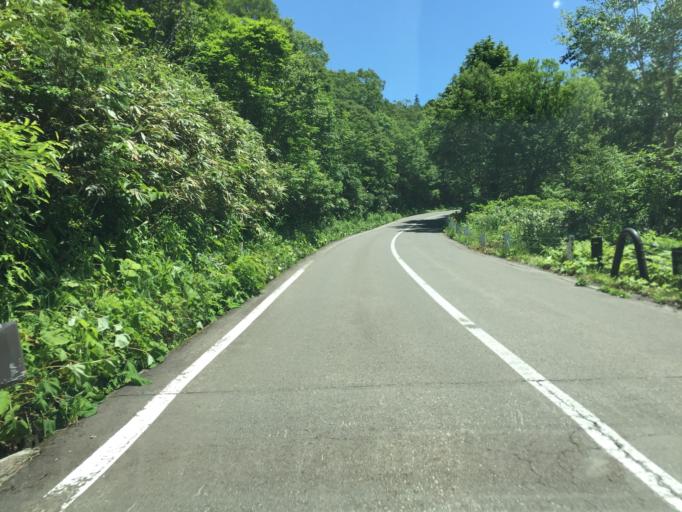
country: JP
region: Fukushima
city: Inawashiro
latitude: 37.6888
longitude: 140.2344
